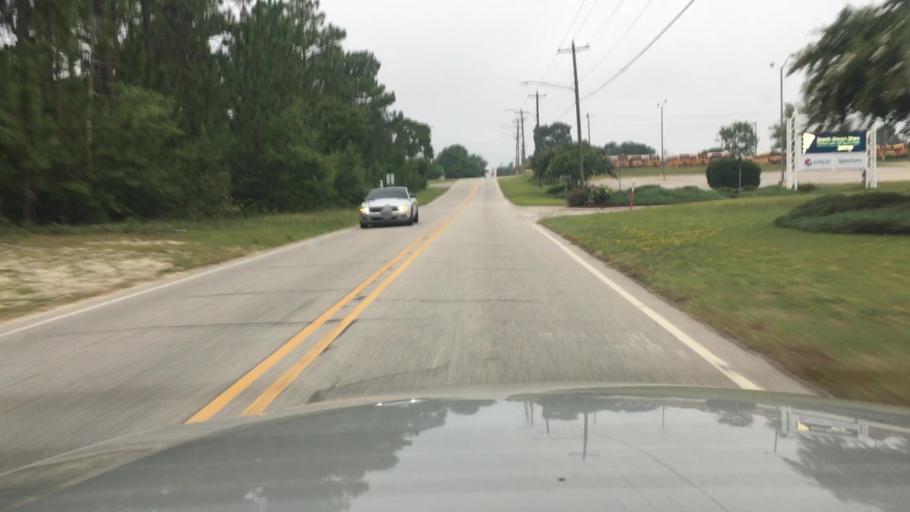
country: US
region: North Carolina
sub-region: Cumberland County
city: Fayetteville
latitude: 35.0123
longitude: -78.8921
